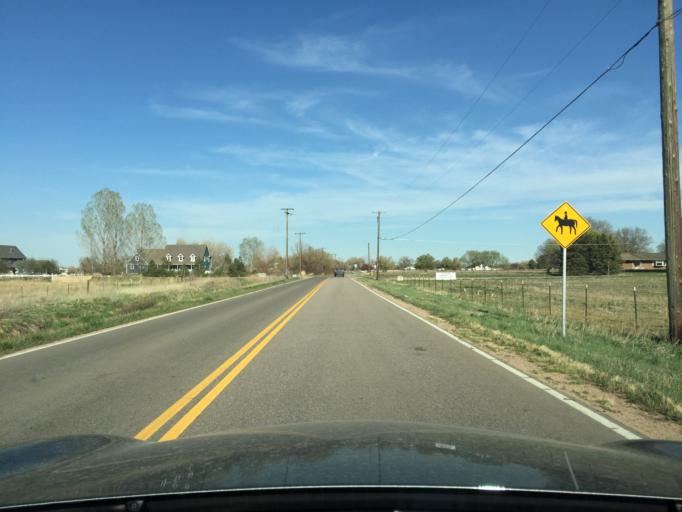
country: US
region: Colorado
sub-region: Boulder County
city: Erie
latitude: 40.0546
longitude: -105.0995
